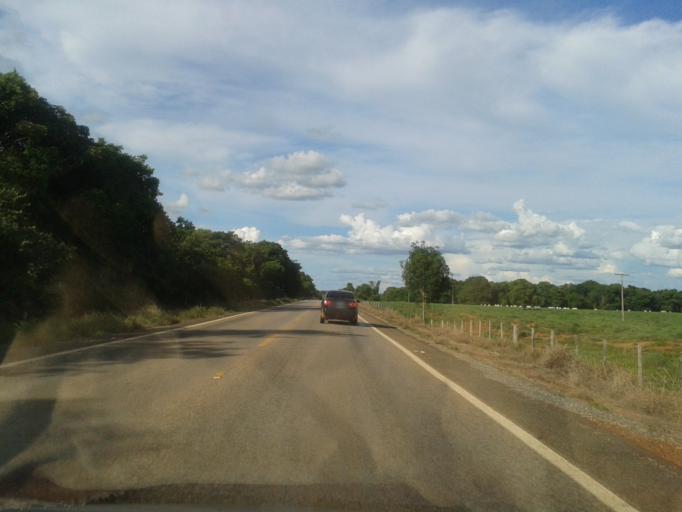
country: BR
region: Goias
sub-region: Mozarlandia
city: Mozarlandia
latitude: -14.3191
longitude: -50.4092
